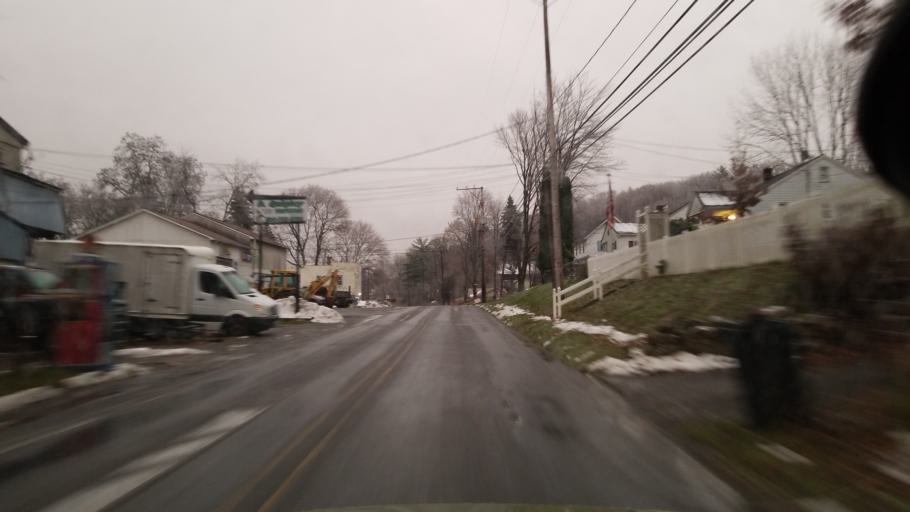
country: US
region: Pennsylvania
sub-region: Clearfield County
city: Clearfield
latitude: 41.0415
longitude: -78.4587
